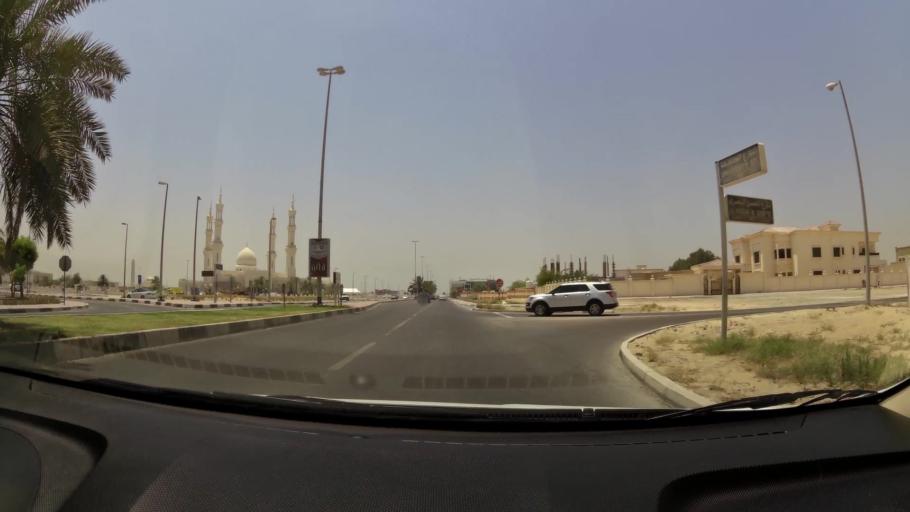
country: AE
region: Ajman
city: Ajman
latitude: 25.4170
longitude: 55.4920
